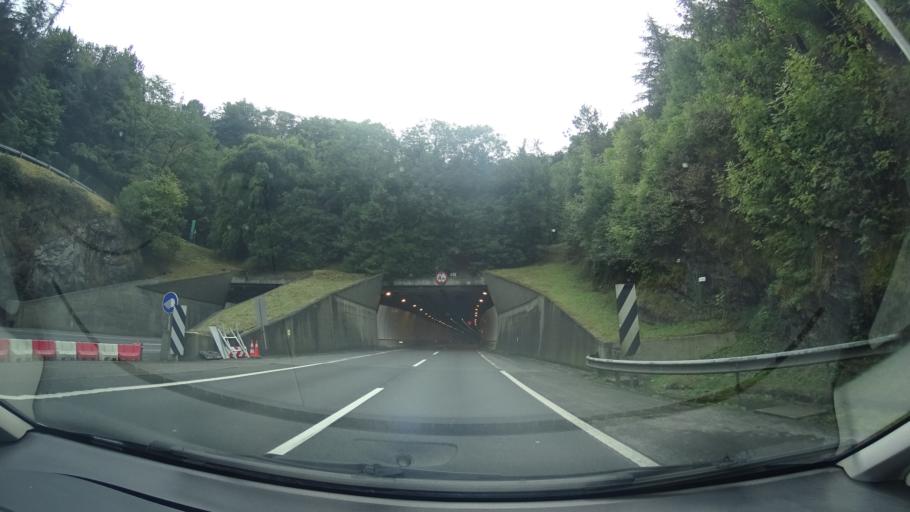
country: ES
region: Basque Country
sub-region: Bizkaia
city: Santutxu
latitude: 43.2335
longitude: -2.9073
